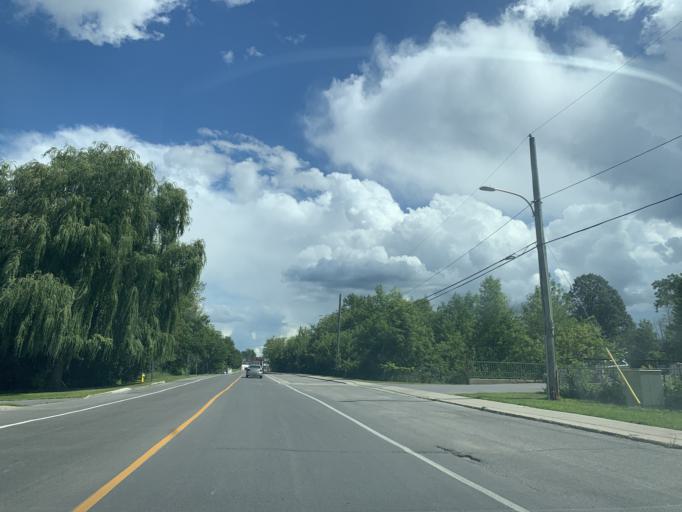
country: CA
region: Ontario
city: Hawkesbury
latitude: 45.6077
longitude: -74.6187
